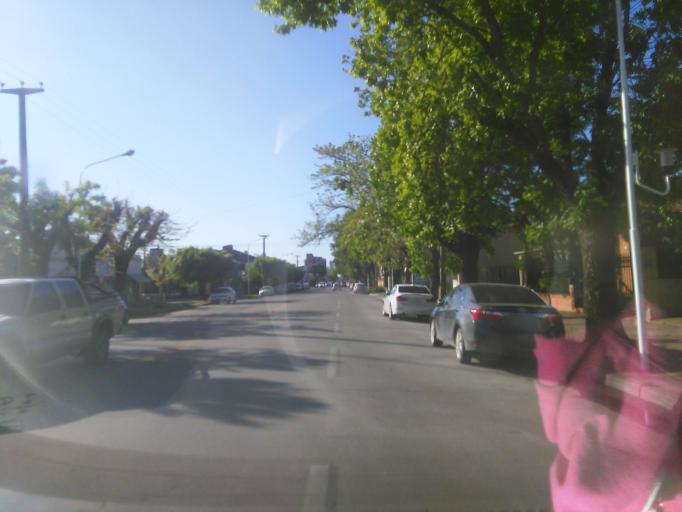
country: AR
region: Buenos Aires
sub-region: Partido de Tandil
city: Tandil
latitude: -37.3332
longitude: -59.1253
